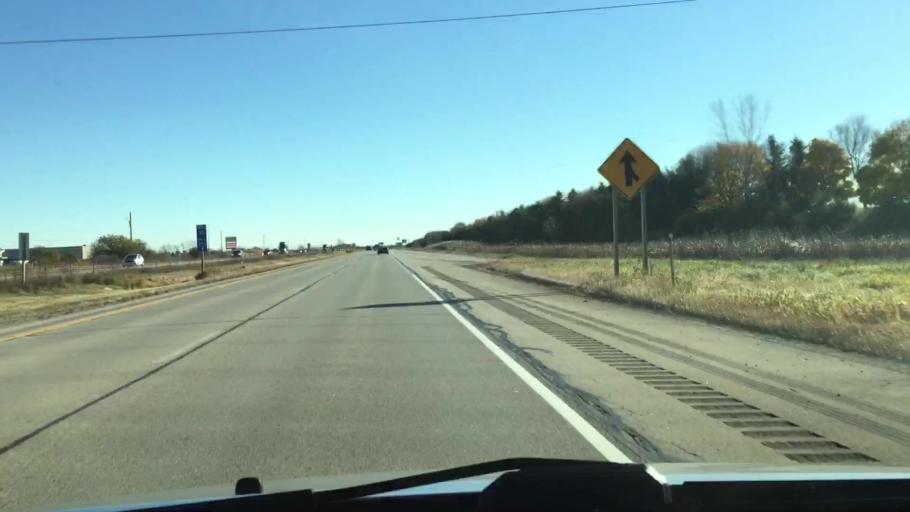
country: US
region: Wisconsin
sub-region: Outagamie County
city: Kimberly
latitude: 44.2979
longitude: -88.3531
